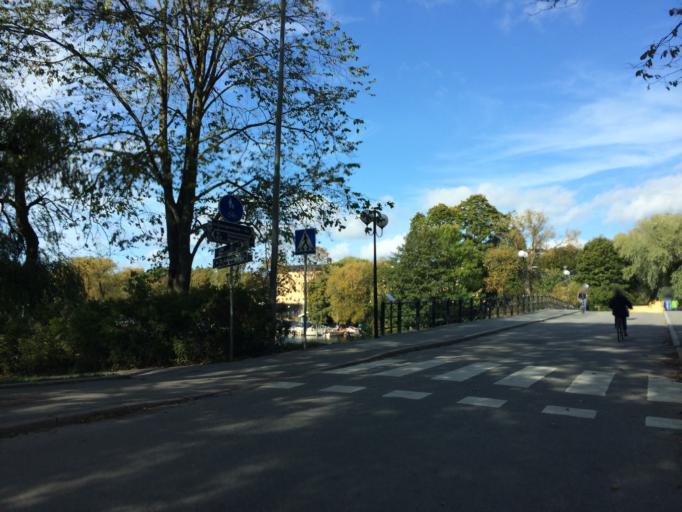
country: SE
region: Stockholm
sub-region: Stockholms Kommun
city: Arsta
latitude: 59.3189
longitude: 18.0283
